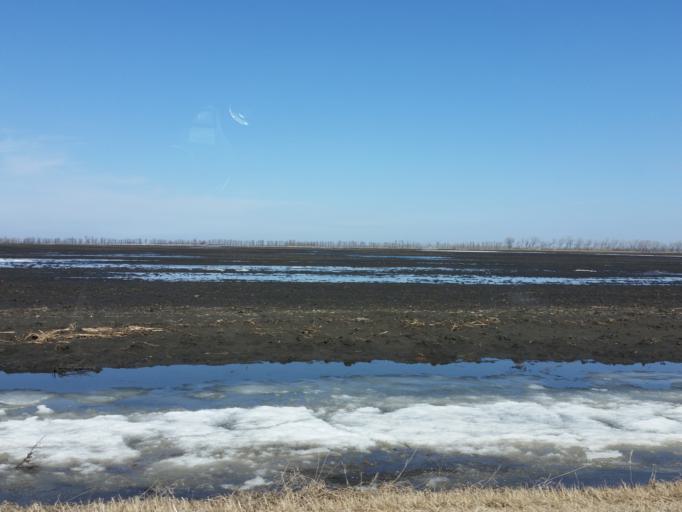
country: US
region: North Dakota
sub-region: Walsh County
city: Grafton
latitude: 48.4266
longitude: -97.2606
